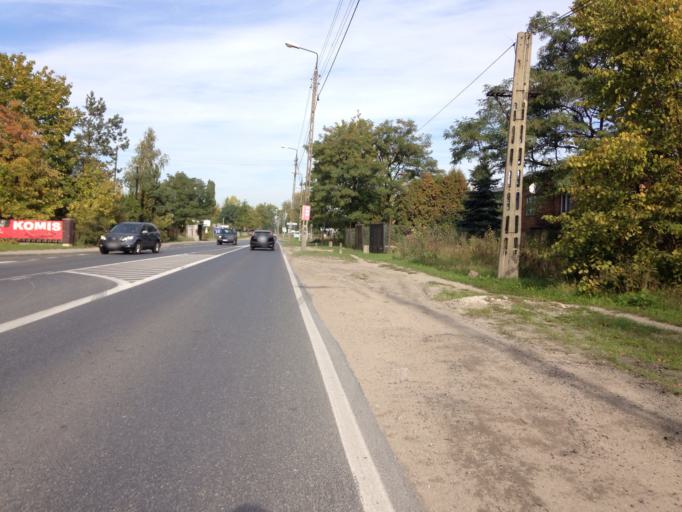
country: PL
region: Masovian Voivodeship
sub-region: Powiat wolominski
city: Zabki
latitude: 52.2685
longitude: 21.1203
